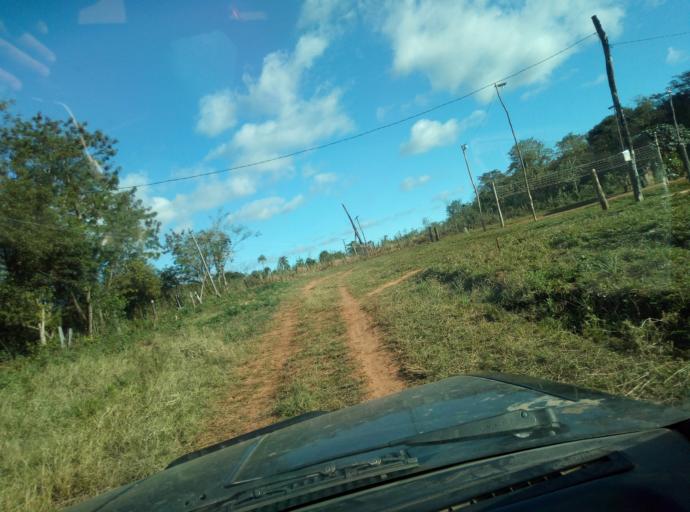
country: PY
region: Caaguazu
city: Carayao
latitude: -25.1738
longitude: -56.2735
